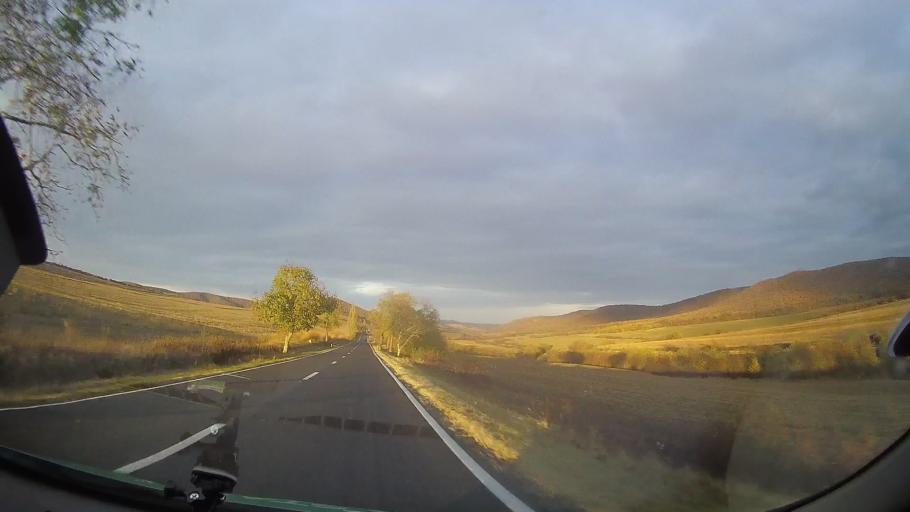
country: RO
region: Tulcea
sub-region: Comuna Ciucurova
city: Ciucurova
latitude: 44.9355
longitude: 28.4890
